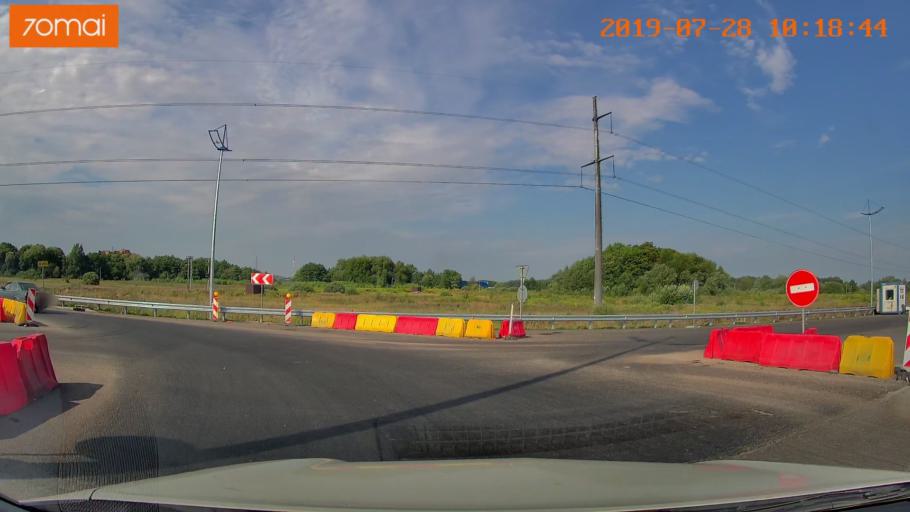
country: RU
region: Kaliningrad
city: Maloye Isakovo
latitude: 54.7528
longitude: 20.5863
